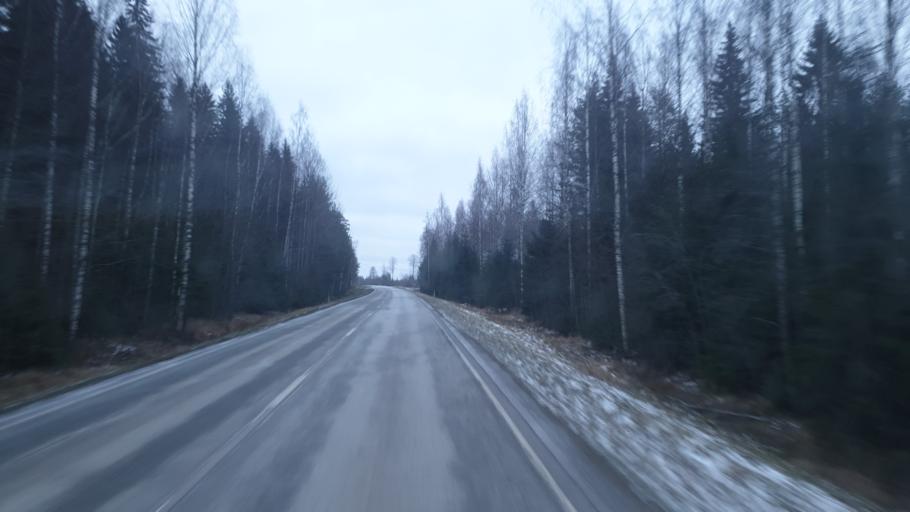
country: FI
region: Southern Savonia
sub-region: Savonlinna
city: Rantasalmi
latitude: 62.0063
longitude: 28.4205
